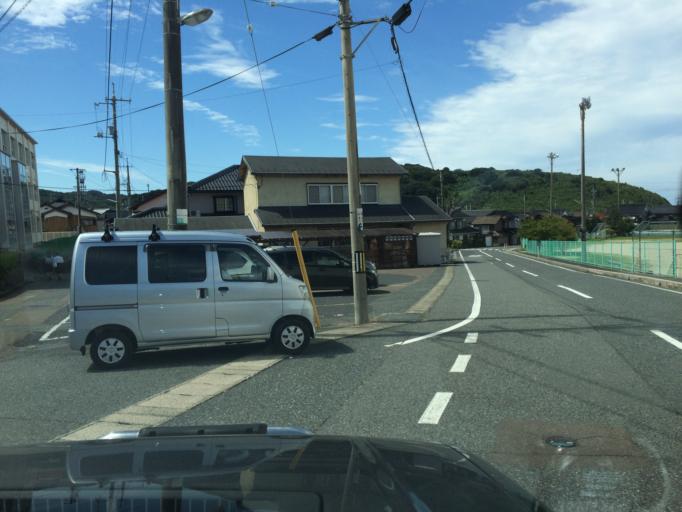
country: JP
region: Tottori
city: Kurayoshi
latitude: 35.5227
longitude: 134.0004
